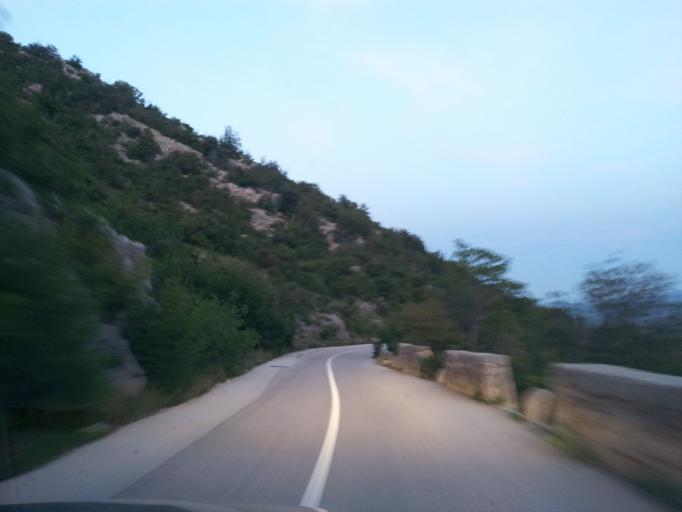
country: HR
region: Zadarska
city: Obrovac
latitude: 44.2392
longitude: 15.6687
